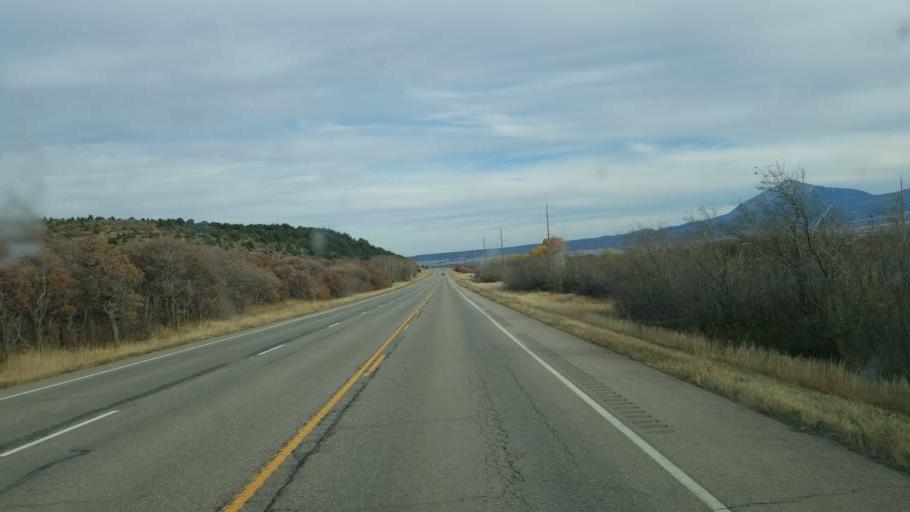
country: US
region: Colorado
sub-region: Huerfano County
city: Walsenburg
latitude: 37.5490
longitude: -105.0970
